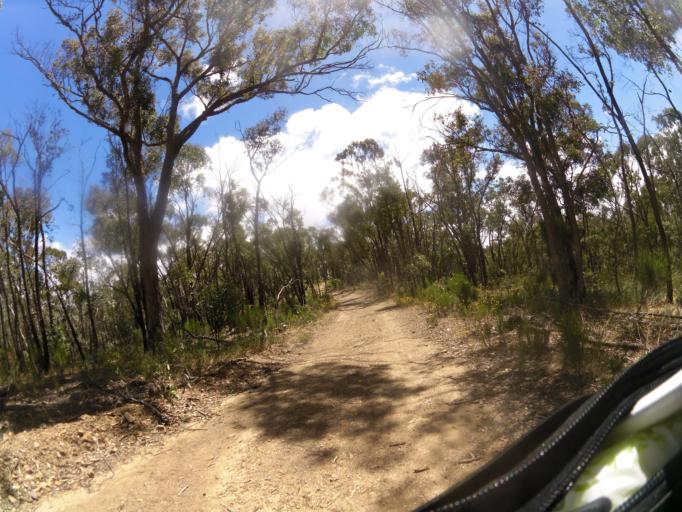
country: AU
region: Victoria
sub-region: Mount Alexander
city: Castlemaine
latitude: -37.0694
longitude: 144.2650
